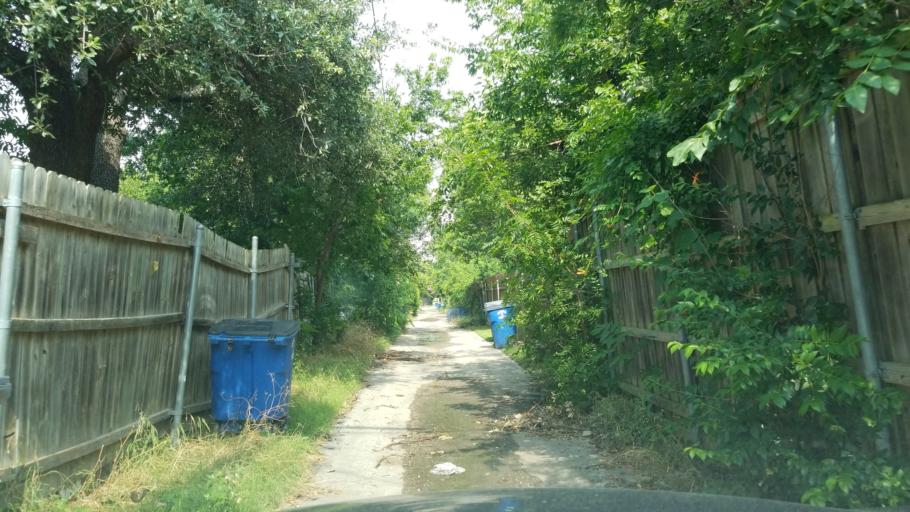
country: US
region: Texas
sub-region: Dallas County
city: Farmers Branch
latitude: 32.9008
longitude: -96.8768
